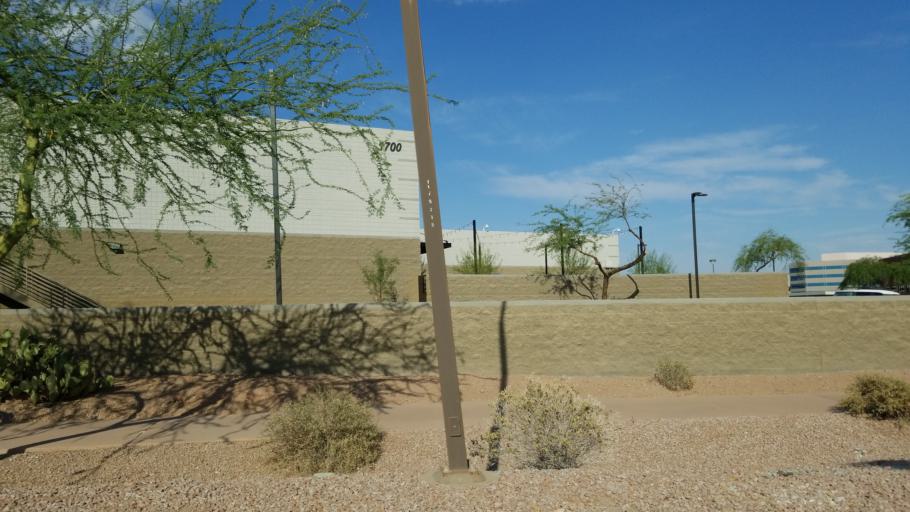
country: US
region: Arizona
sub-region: Maricopa County
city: Tempe Junction
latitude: 33.4468
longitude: -111.9610
